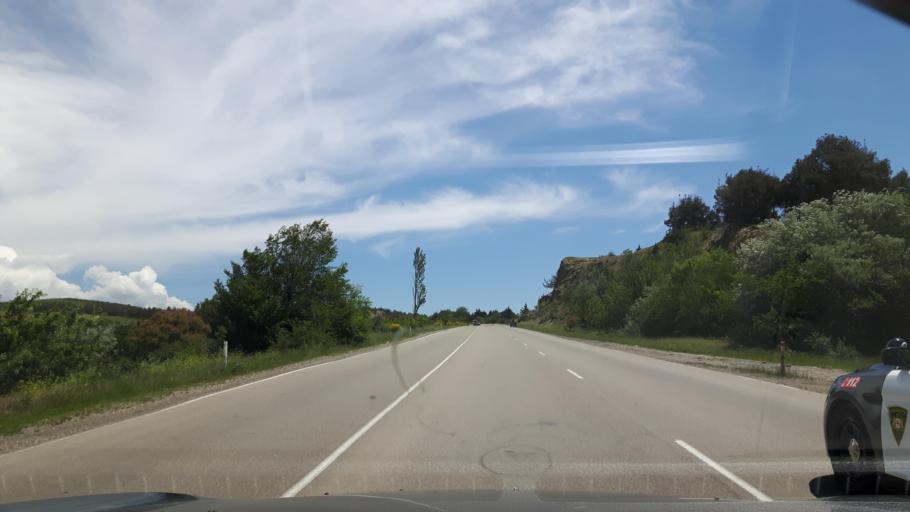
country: GE
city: Didi Lilo
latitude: 41.6925
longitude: 45.0741
